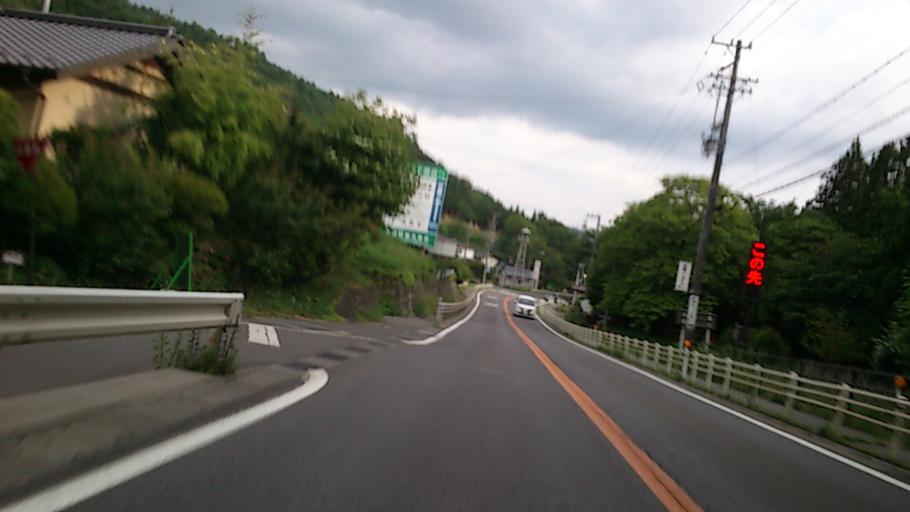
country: JP
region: Nagano
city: Suwa
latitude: 36.1232
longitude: 138.1023
